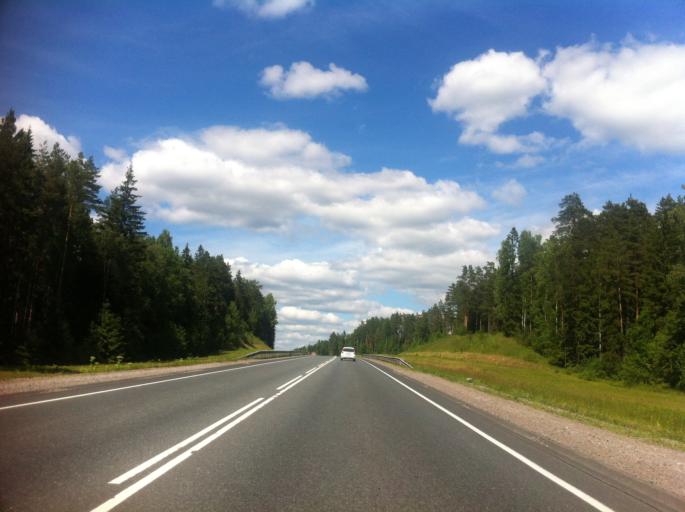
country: RU
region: Leningrad
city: Luga
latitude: 58.6663
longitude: 29.8665
